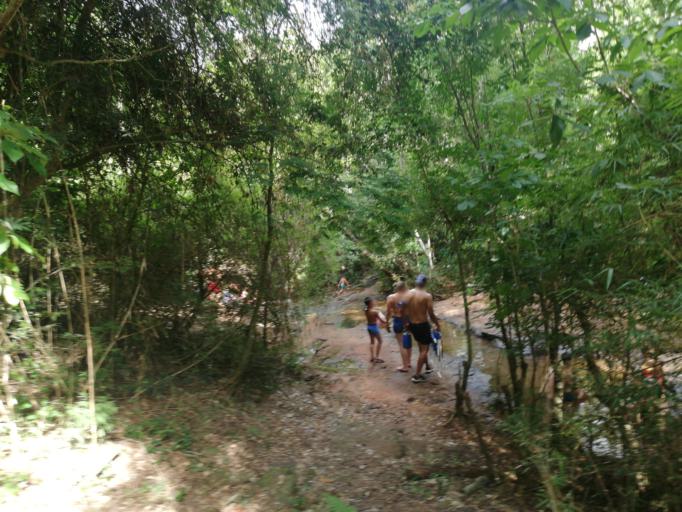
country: AR
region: Misiones
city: Cerro Azul
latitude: -27.6294
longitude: -55.4922
